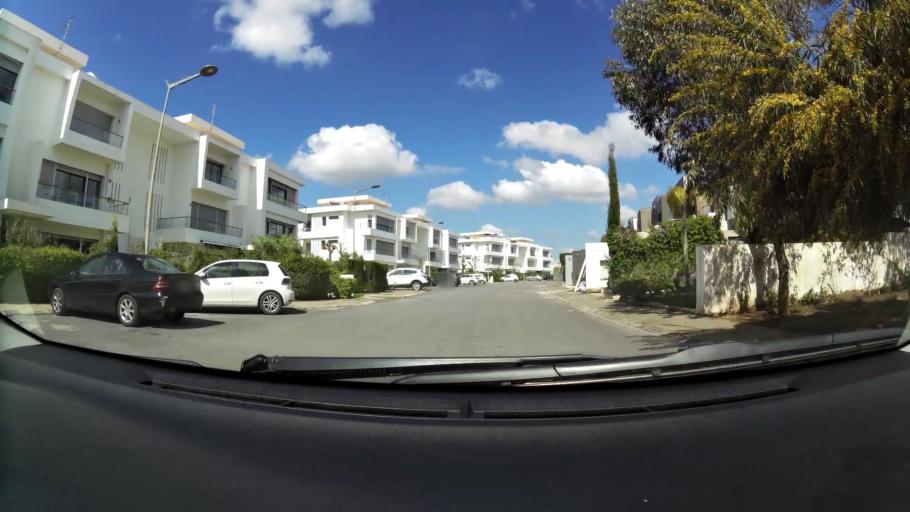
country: MA
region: Grand Casablanca
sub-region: Nouaceur
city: Bouskoura
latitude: 33.4694
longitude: -7.6036
